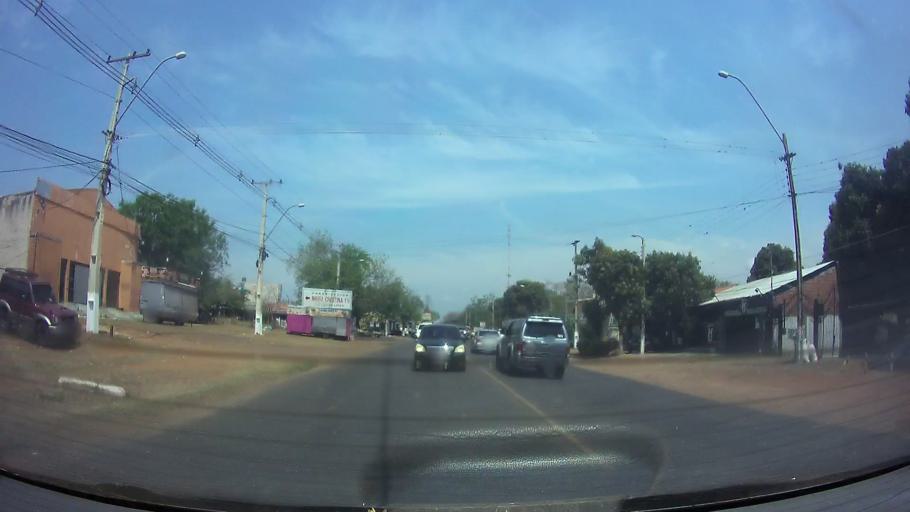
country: PY
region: Central
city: Capiata
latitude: -25.3990
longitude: -57.4653
